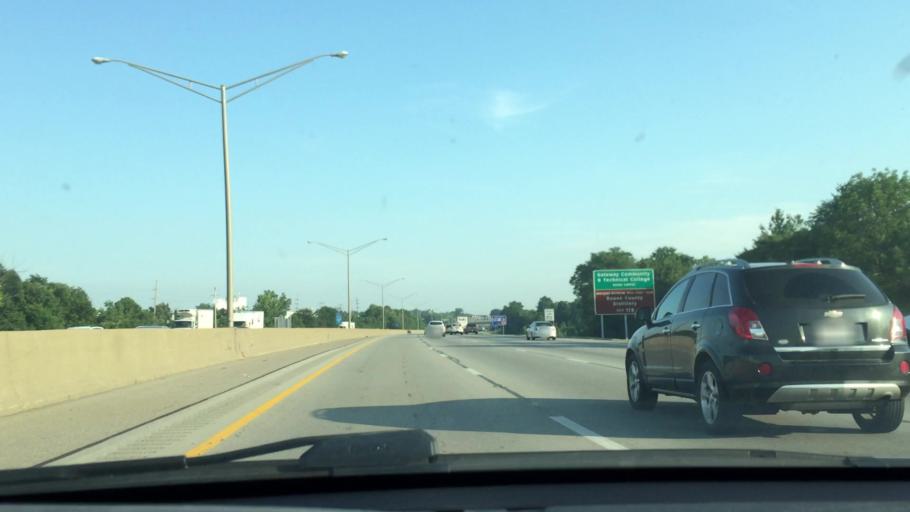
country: US
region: Kentucky
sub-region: Boone County
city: Florence
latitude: 38.9736
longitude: -84.6373
